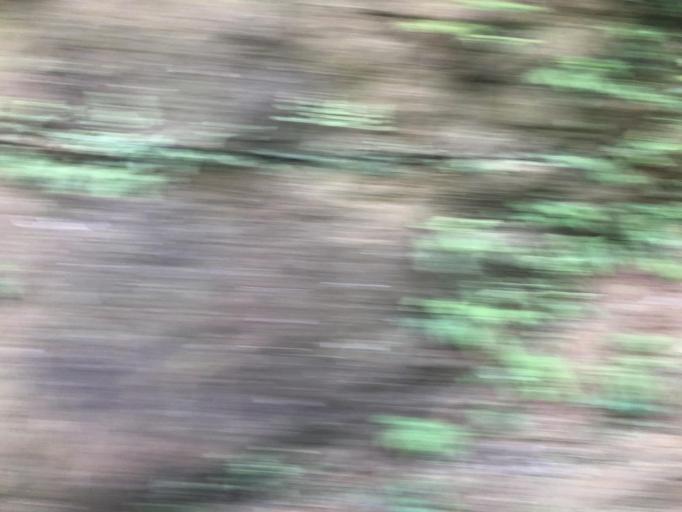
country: TW
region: Taiwan
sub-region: Keelung
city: Keelung
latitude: 25.2029
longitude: 121.6470
